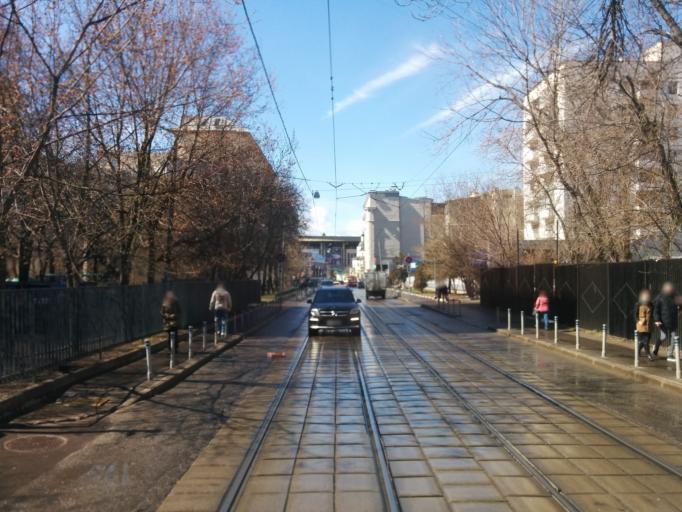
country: RU
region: Moscow
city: Mar'ina Roshcha
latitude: 55.7802
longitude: 37.6362
